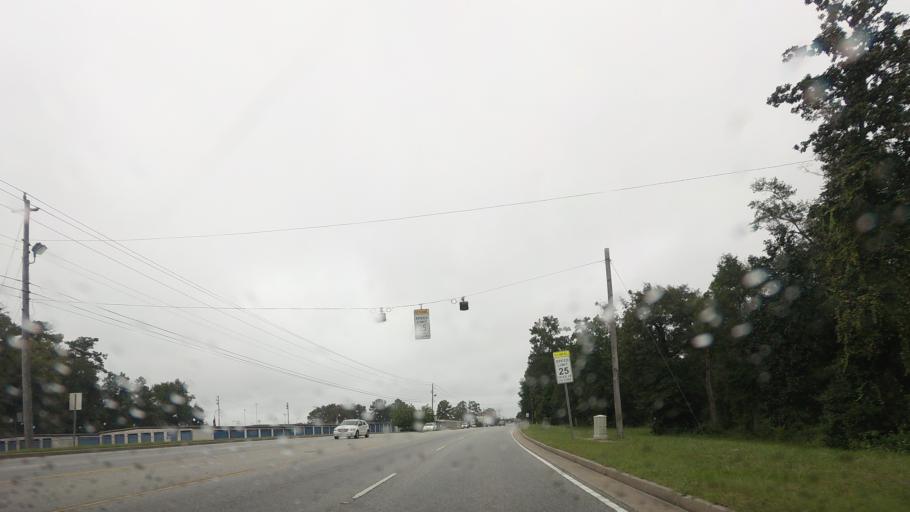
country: US
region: Georgia
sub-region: Lowndes County
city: Remerton
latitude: 30.8324
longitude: -83.3206
